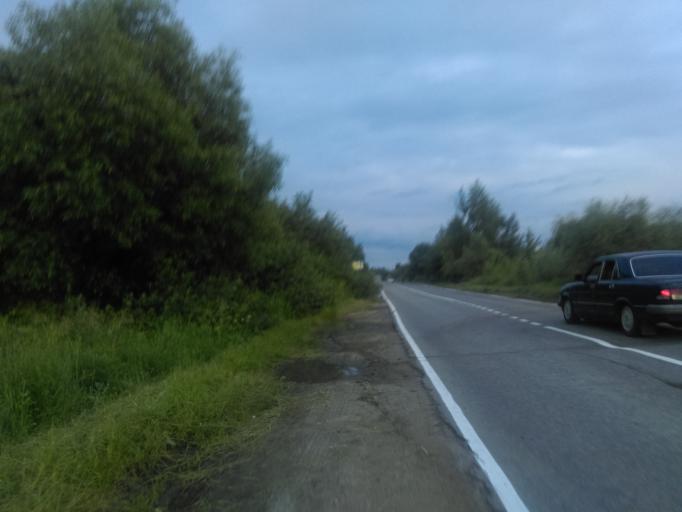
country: RU
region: Moskovskaya
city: Vostryakovo
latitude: 55.3923
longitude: 37.8062
